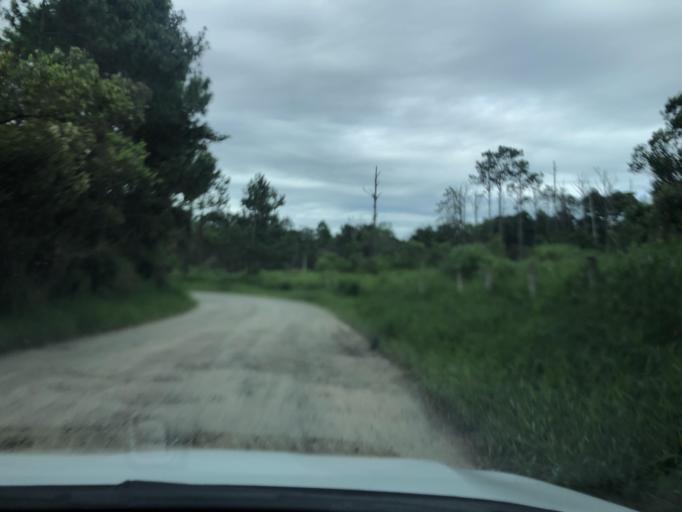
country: BR
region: Santa Catarina
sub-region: Florianopolis
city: Lagoa
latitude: -27.5512
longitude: -48.4395
